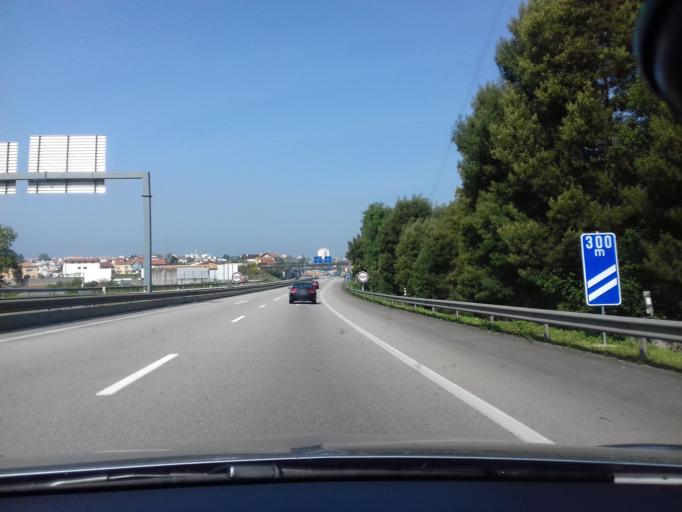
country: PT
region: Aveiro
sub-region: Espinho
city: Silvalde
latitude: 41.0083
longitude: -8.6122
